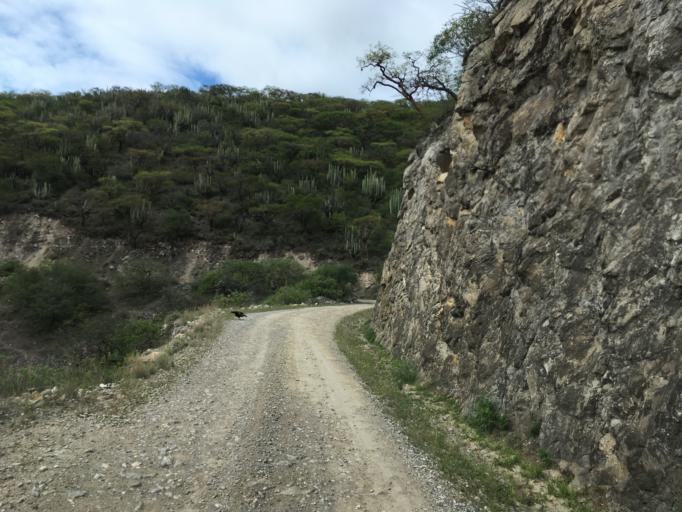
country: MX
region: Hidalgo
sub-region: Metztitlan
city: Fontezuelas
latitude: 20.6416
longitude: -98.9356
